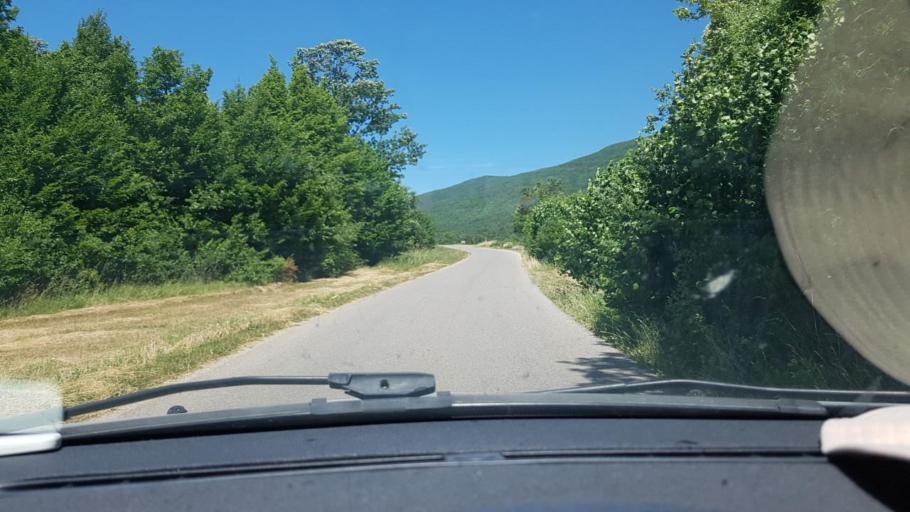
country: HR
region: Licko-Senjska
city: Otocac
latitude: 44.8034
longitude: 15.3634
